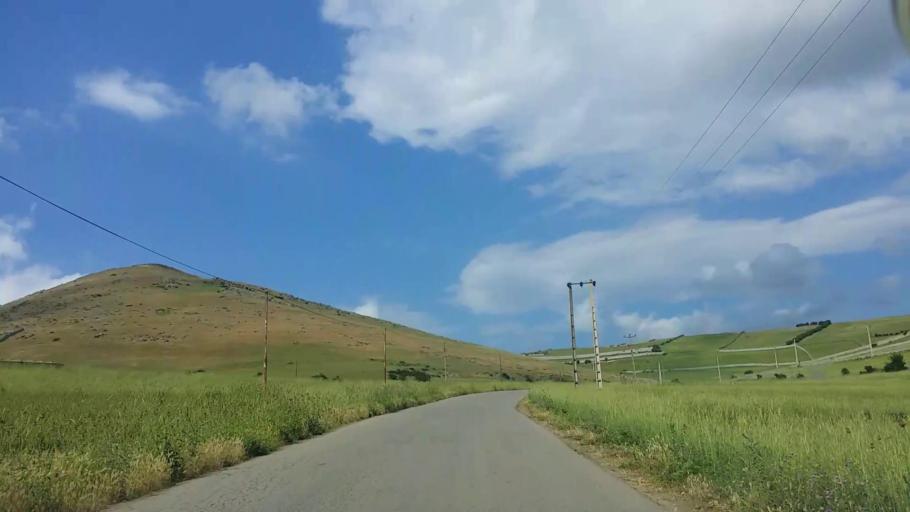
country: IR
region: Mazandaran
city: Chalus
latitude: 36.5247
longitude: 51.2638
